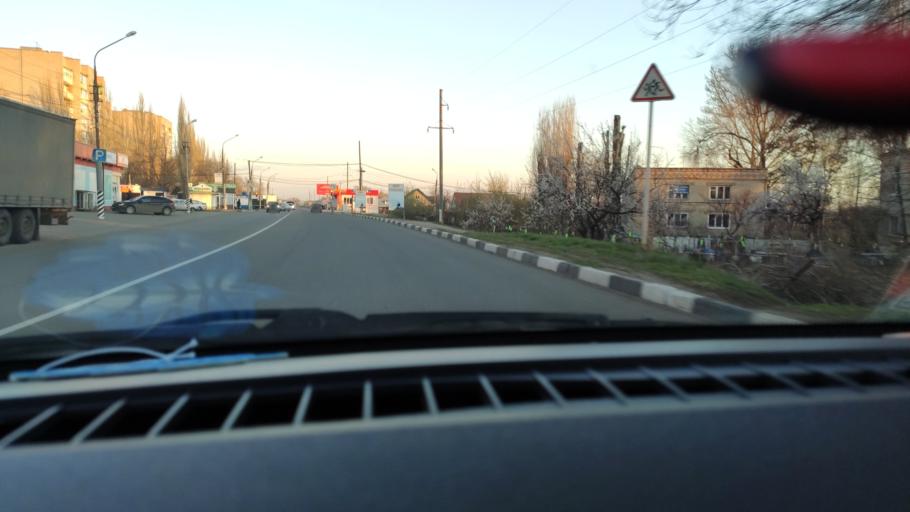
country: RU
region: Saratov
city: Privolzhskiy
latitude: 51.3902
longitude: 46.0359
